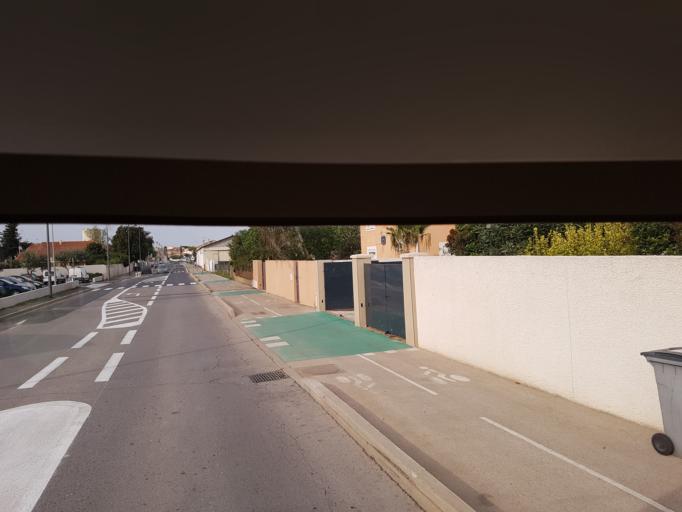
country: FR
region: Languedoc-Roussillon
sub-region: Departement de l'Herault
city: Marseillan
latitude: 43.3575
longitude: 3.5225
